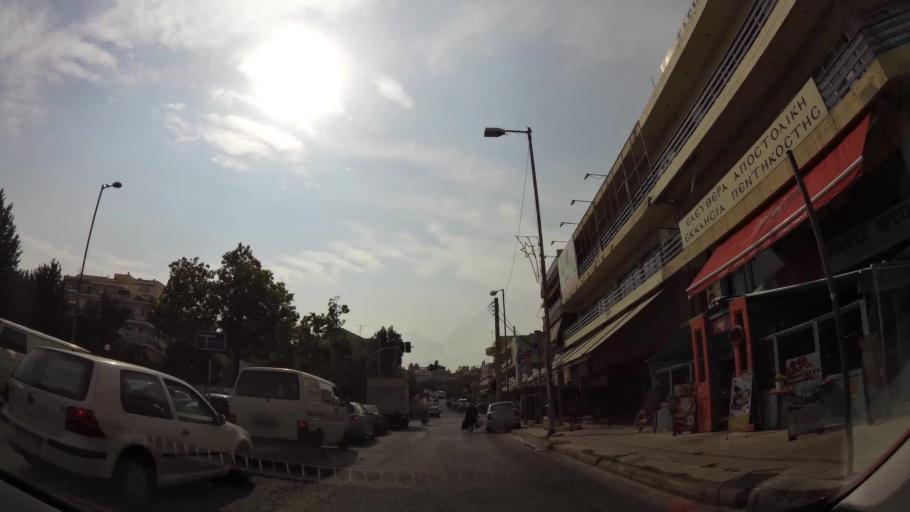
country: GR
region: Attica
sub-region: Nomarchia Athinas
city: Peristeri
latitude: 38.0125
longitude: 23.6861
